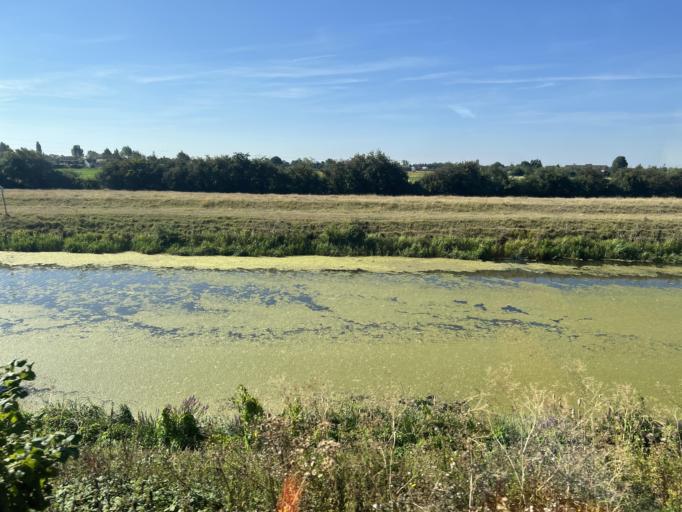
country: GB
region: England
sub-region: Lincolnshire
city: Kirton
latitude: 52.9758
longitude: -0.1171
